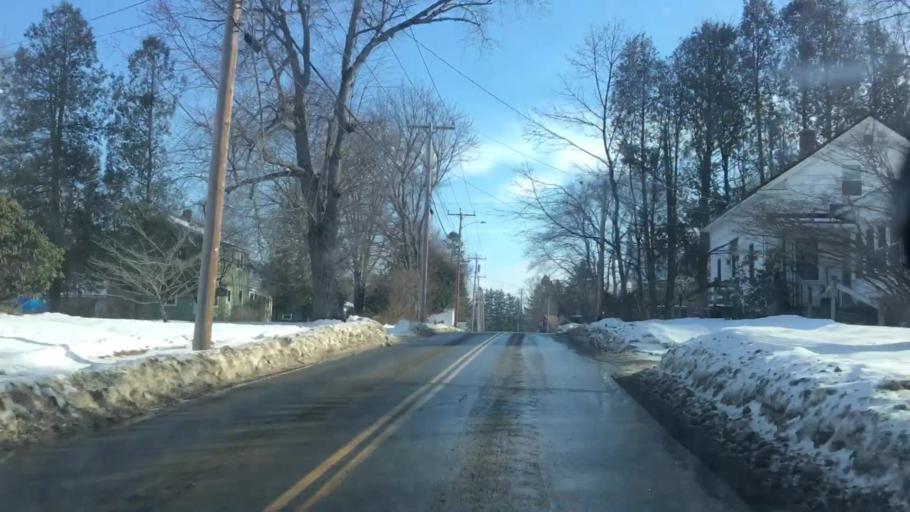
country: US
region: Maine
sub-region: Penobscot County
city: Brewer
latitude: 44.7686
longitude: -68.7761
